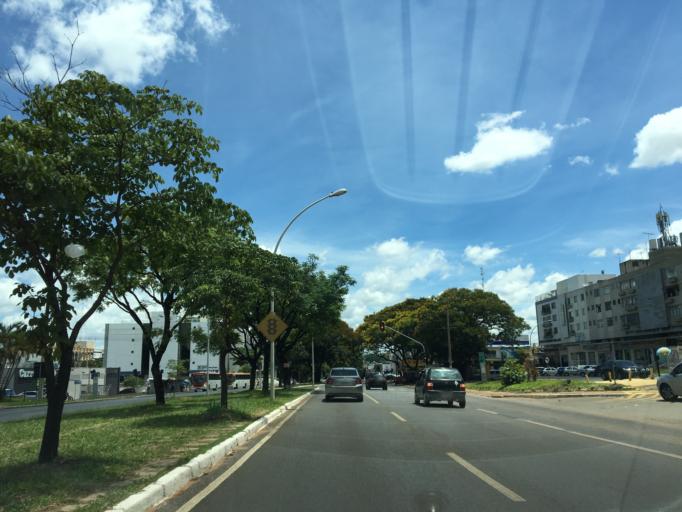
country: BR
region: Federal District
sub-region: Brasilia
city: Brasilia
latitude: -15.7498
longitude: -47.8955
